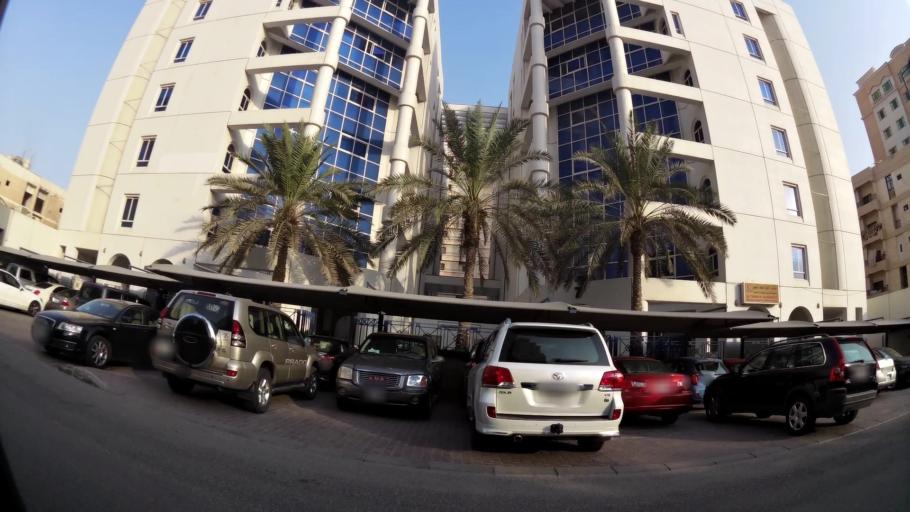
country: KW
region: Muhafazat Hawalli
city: As Salimiyah
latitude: 29.3363
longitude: 48.0608
